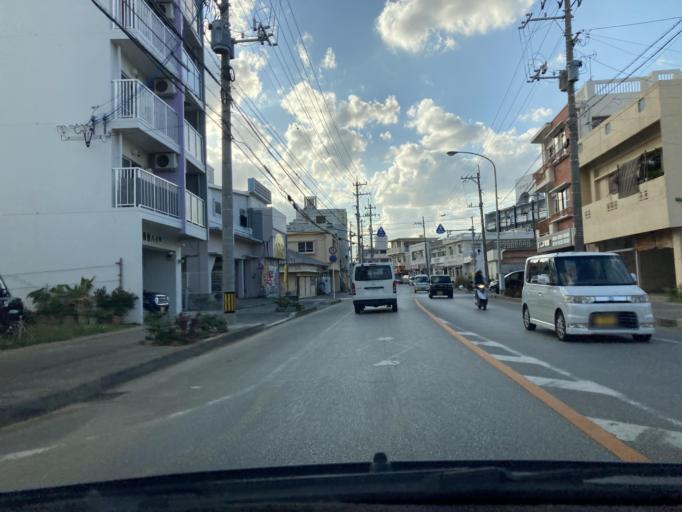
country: JP
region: Okinawa
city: Chatan
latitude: 26.3202
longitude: 127.7840
